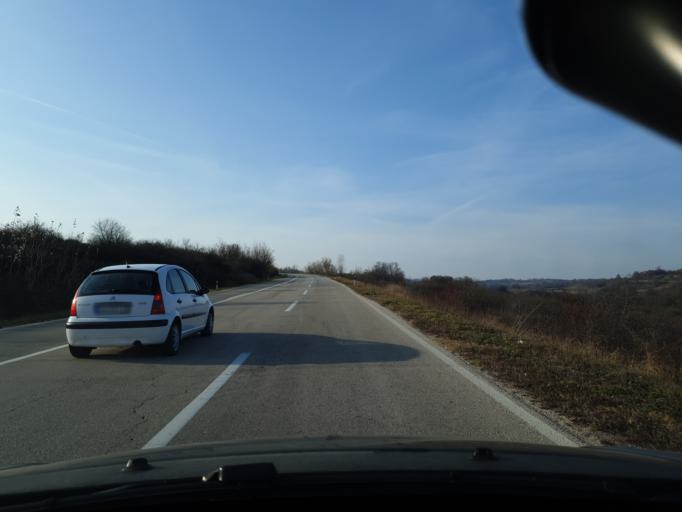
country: RS
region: Central Serbia
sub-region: Zajecarski Okrug
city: Zajecar
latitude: 43.9572
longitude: 22.2734
